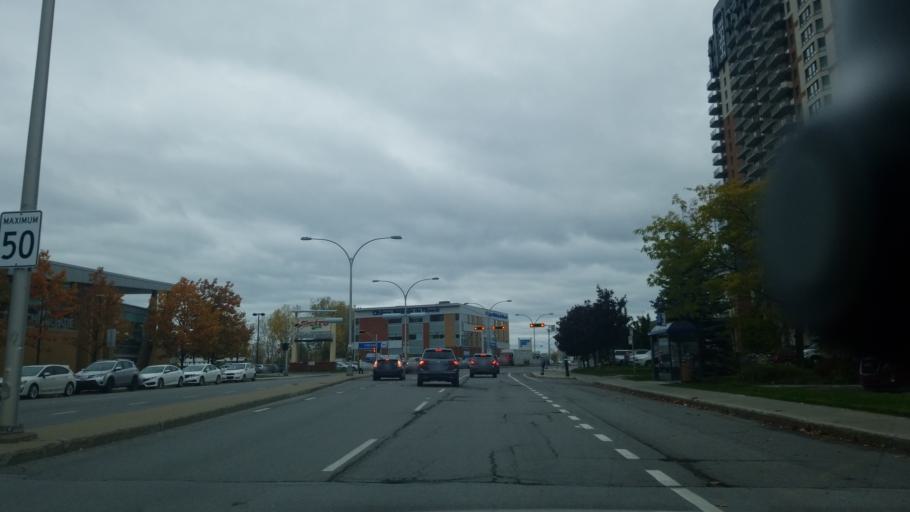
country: CA
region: Quebec
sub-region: Laval
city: Laval
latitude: 45.5623
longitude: -73.7230
